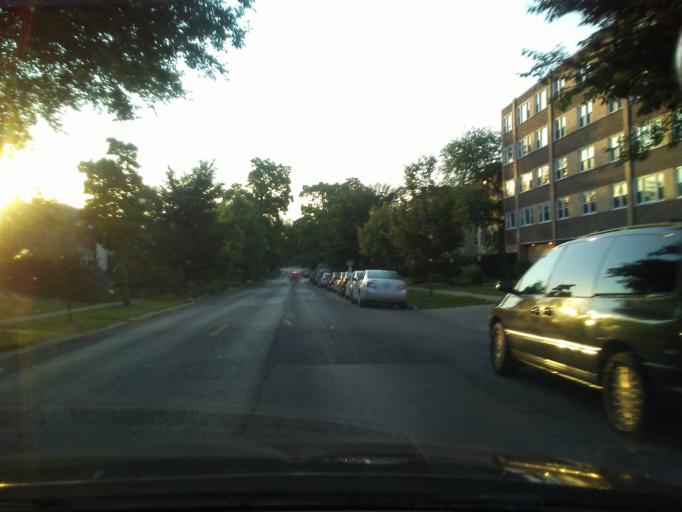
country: US
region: Illinois
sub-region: Cook County
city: Evanston
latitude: 42.0266
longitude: -87.6820
